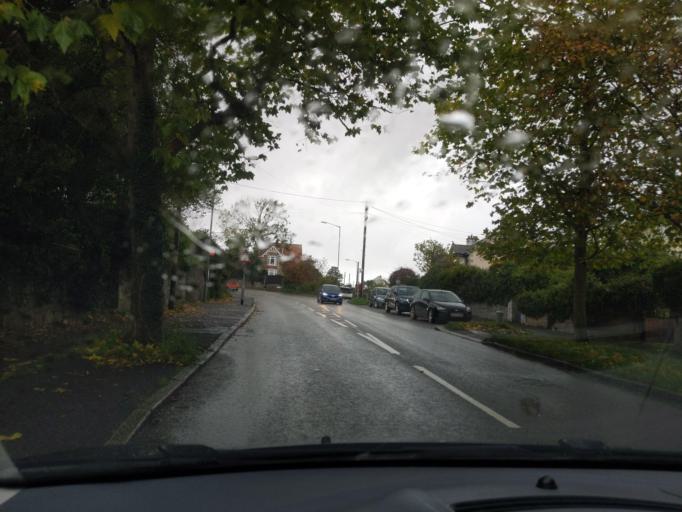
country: GB
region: England
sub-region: Cornwall
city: Wadebridge
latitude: 50.5175
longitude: -4.8438
